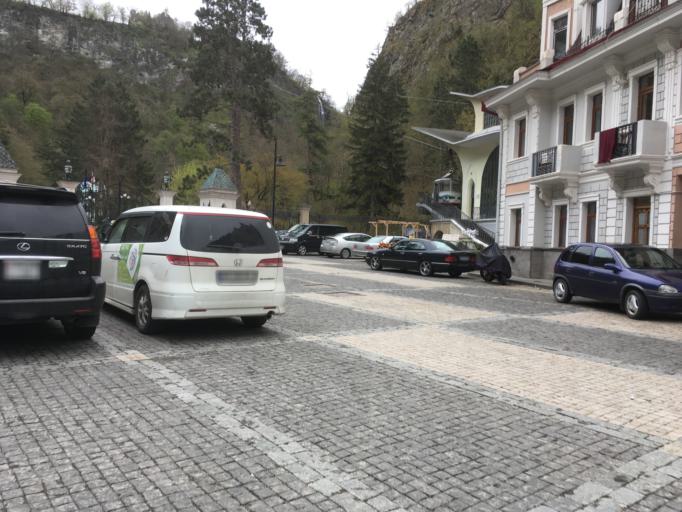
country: GE
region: Samtskhe-Javakheti
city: Borjomi
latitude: 41.8364
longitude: 43.3903
